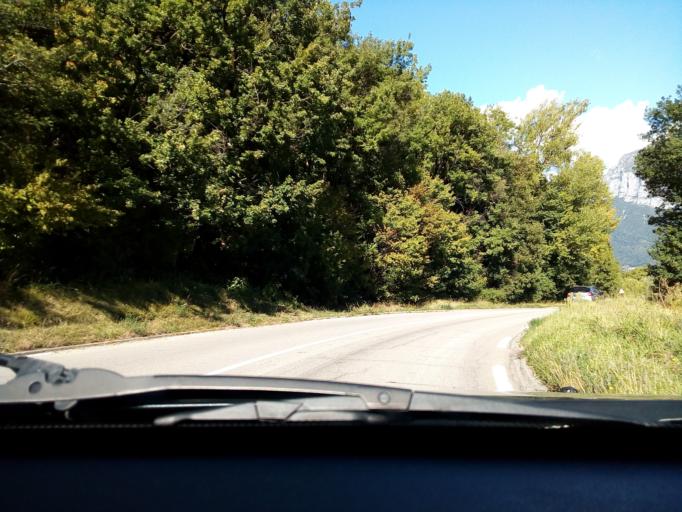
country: FR
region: Rhone-Alpes
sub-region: Departement de l'Isere
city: Sassenage
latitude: 45.2167
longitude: 5.6457
